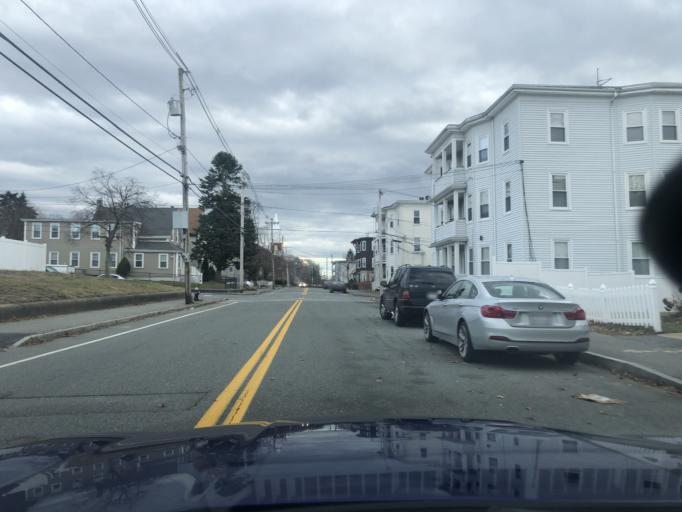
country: US
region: Massachusetts
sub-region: Plymouth County
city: Brockton
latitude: 42.1036
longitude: -71.0131
